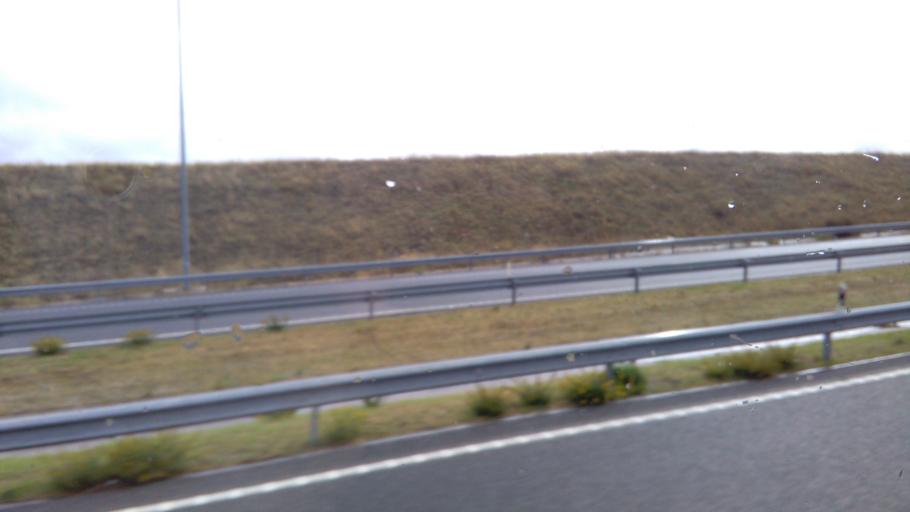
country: ES
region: Madrid
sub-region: Provincia de Madrid
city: Alcorcon
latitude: 40.3300
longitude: -3.8149
